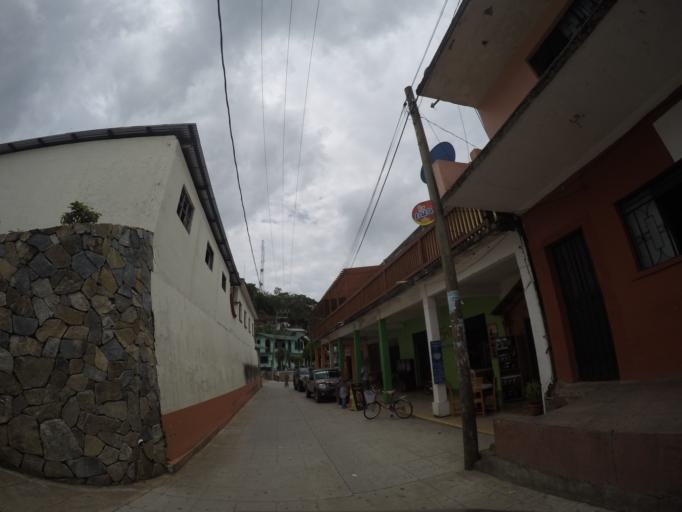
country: MX
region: Oaxaca
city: Pluma Hidalgo
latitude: 15.9254
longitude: -96.4196
